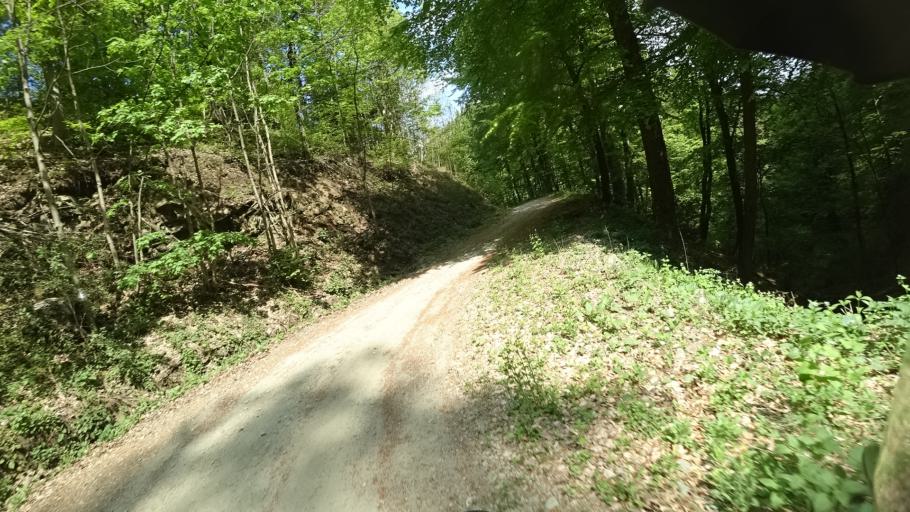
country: HR
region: Grad Zagreb
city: Kasina
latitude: 45.9238
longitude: 16.0129
